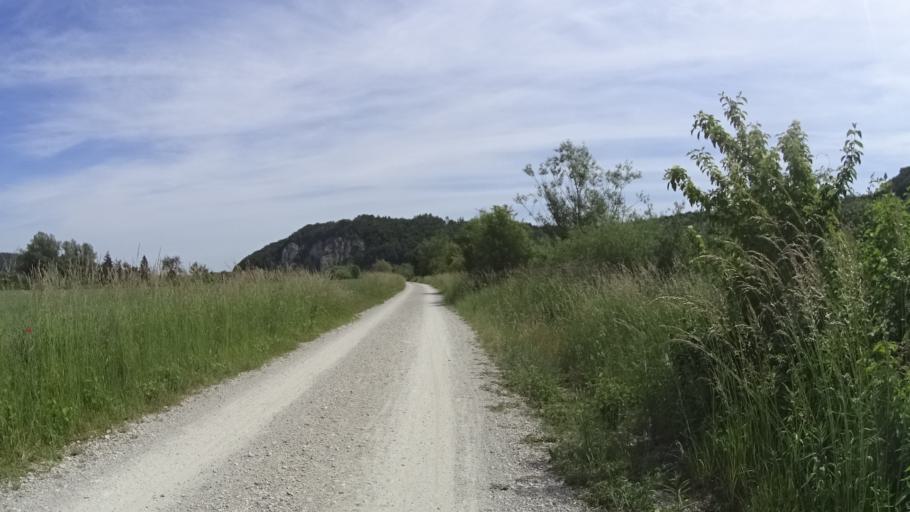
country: DE
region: Bavaria
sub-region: Lower Bavaria
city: Saal
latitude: 48.9075
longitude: 11.9643
